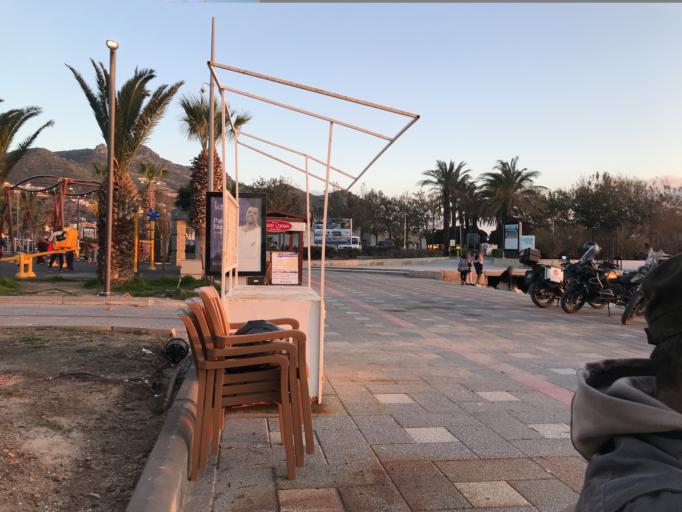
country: TR
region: Mugla
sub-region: Bodrum
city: Karatoprak
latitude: 37.0056
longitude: 27.2568
